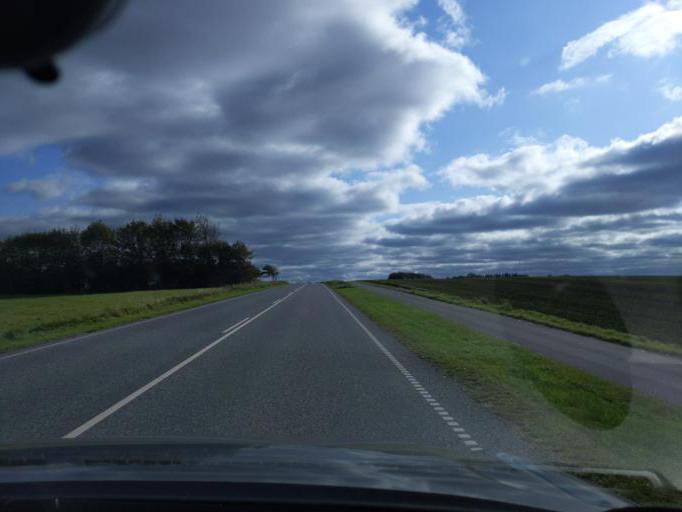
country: DK
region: North Denmark
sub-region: Mariagerfjord Kommune
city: Hobro
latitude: 56.5214
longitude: 9.7323
